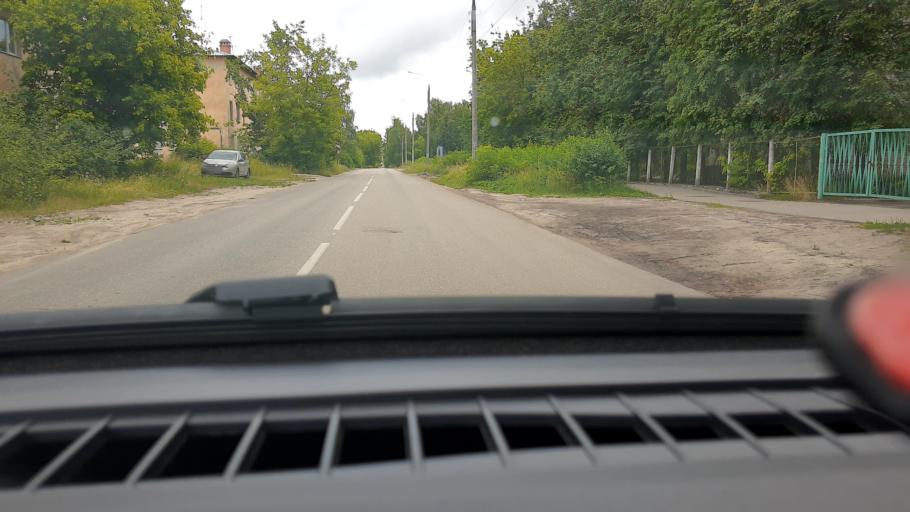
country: RU
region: Nizjnij Novgorod
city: Dzerzhinsk
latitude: 56.2422
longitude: 43.4268
